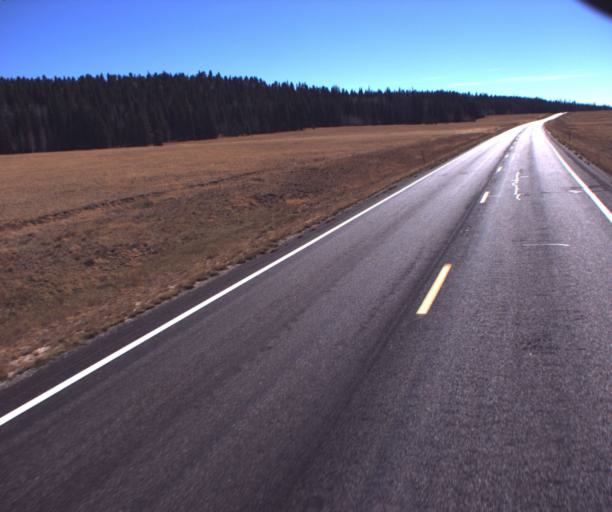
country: US
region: Arizona
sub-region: Coconino County
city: Grand Canyon
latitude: 36.3640
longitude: -112.1201
